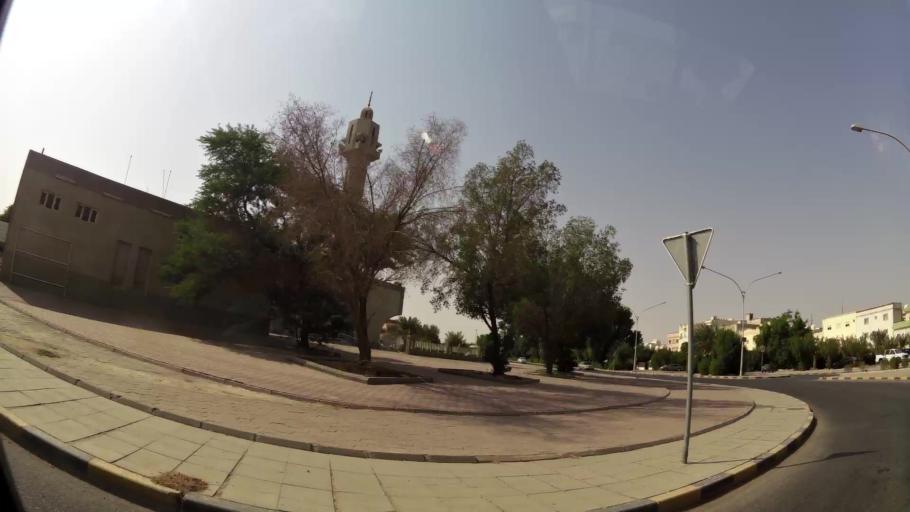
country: KW
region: Muhafazat al Jahra'
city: Al Jahra'
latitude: 29.3303
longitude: 47.6539
